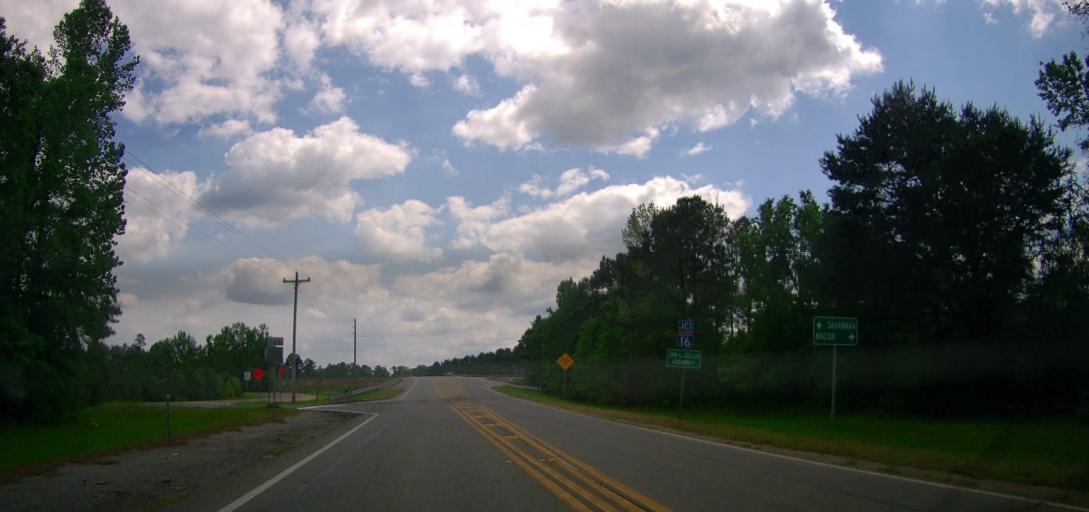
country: US
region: Georgia
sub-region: Laurens County
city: East Dublin
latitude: 32.4750
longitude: -82.8161
